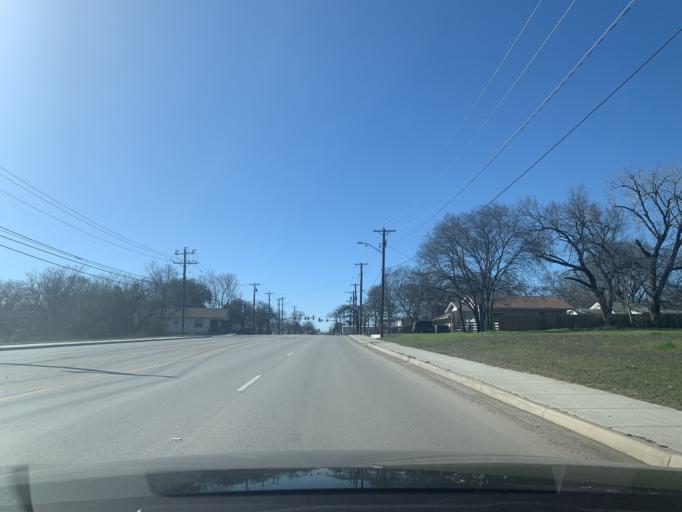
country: US
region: Texas
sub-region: Tarrant County
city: Haltom City
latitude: 32.7653
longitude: -97.2855
